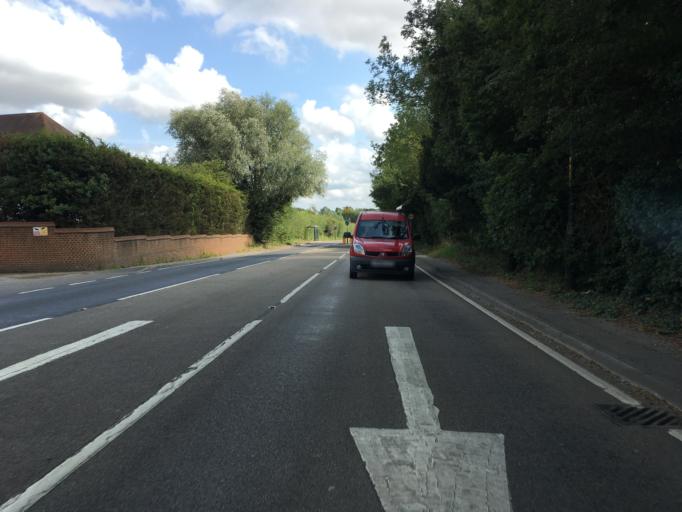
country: GB
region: England
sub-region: Kent
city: Headcorn
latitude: 51.2051
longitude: 0.5915
